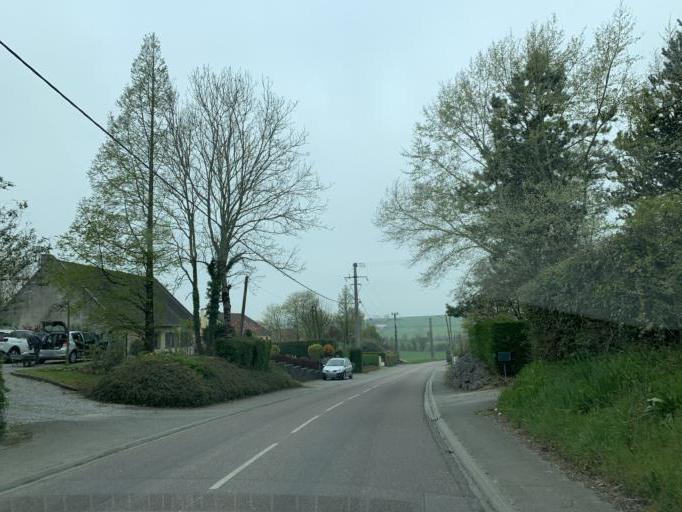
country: FR
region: Nord-Pas-de-Calais
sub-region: Departement du Pas-de-Calais
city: Rinxent
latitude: 50.7808
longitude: 1.7331
